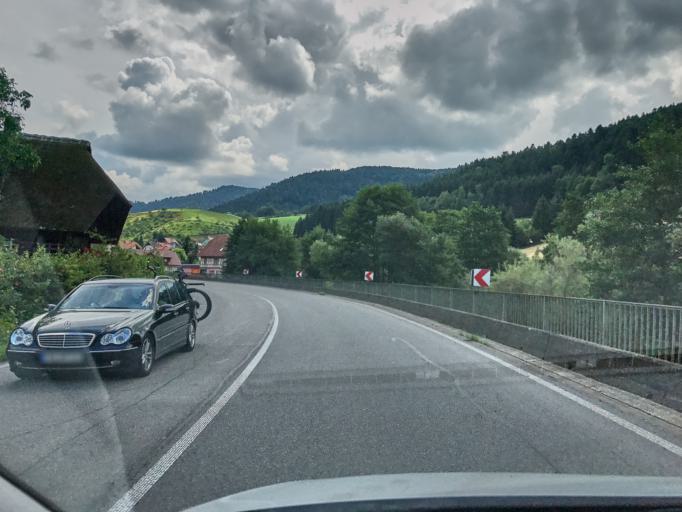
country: DE
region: Baden-Wuerttemberg
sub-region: Freiburg Region
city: Wolfach
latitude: 48.2910
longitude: 8.2630
